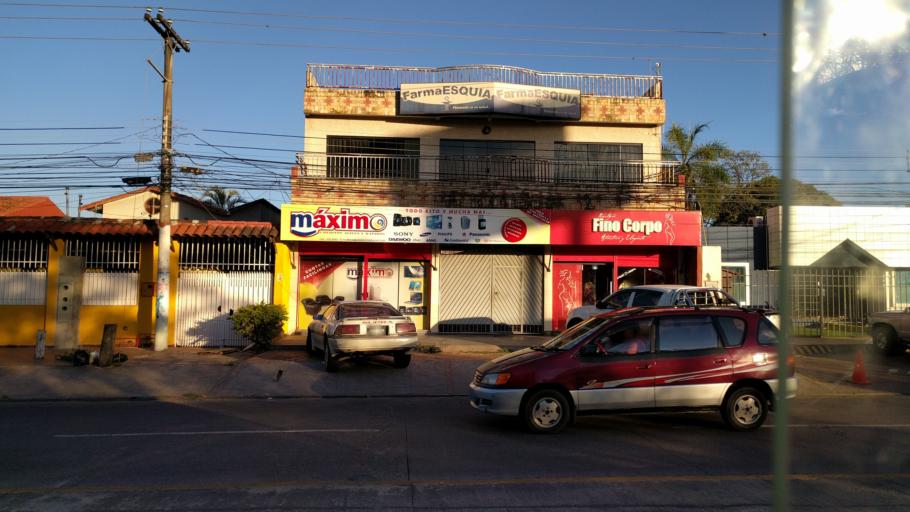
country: BO
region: Santa Cruz
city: Santa Cruz de la Sierra
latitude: -17.7669
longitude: -63.1991
